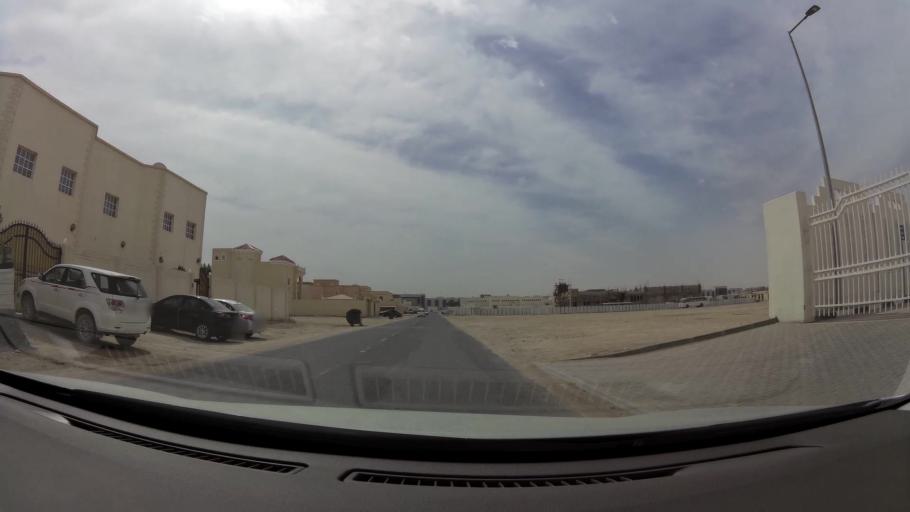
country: QA
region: Al Wakrah
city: Al Wukayr
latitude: 25.2053
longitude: 51.4680
